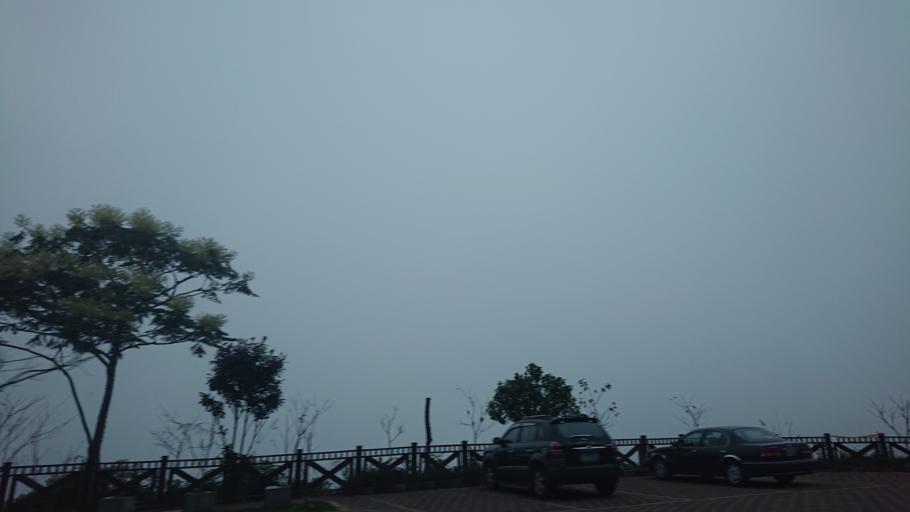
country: TW
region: Taiwan
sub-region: Chiayi
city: Jiayi Shi
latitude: 23.4771
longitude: 120.6953
